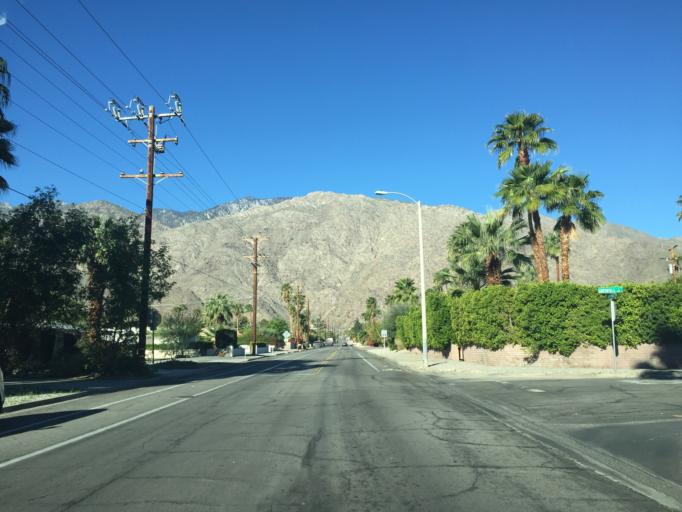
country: US
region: California
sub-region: Riverside County
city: Palm Springs
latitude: 33.8123
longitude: -116.5351
